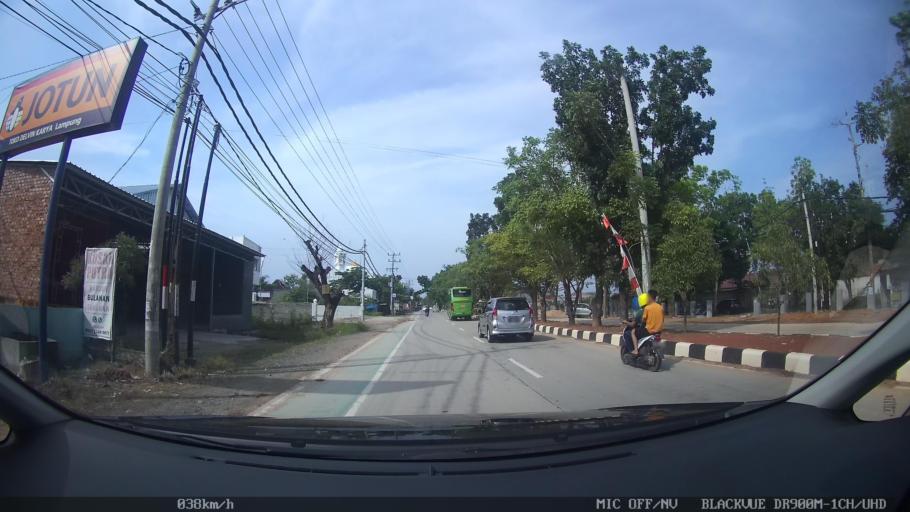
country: ID
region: Lampung
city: Kedaton
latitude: -5.3738
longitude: 105.2965
